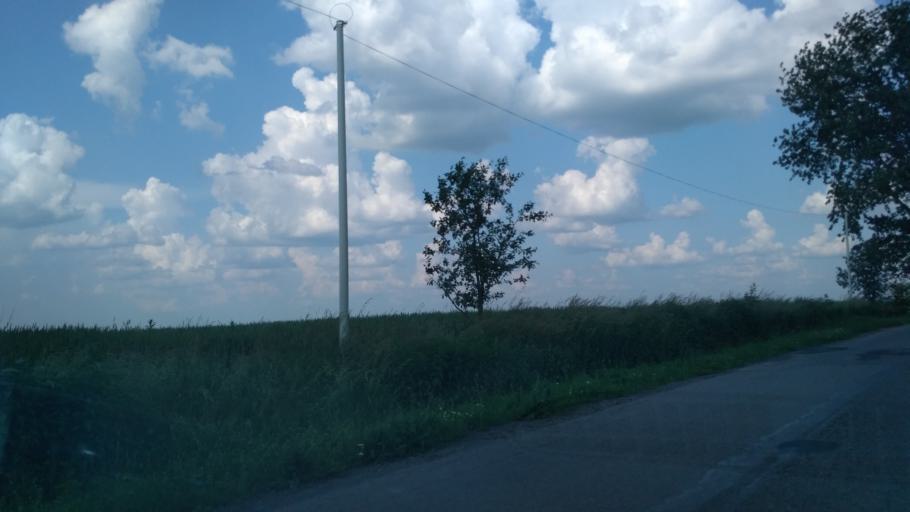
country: PL
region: Subcarpathian Voivodeship
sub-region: Powiat jaroslawski
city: Ostrow
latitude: 49.9433
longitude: 22.7581
